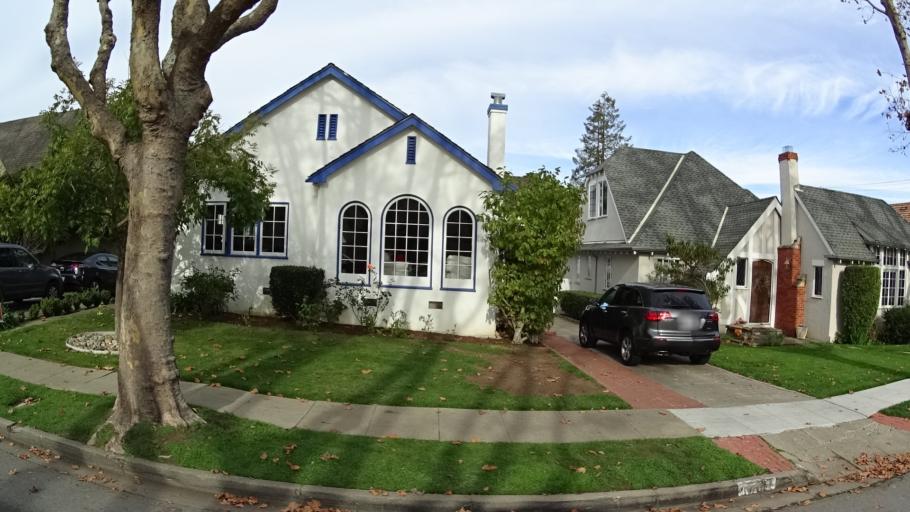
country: US
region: California
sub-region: San Mateo County
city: Burlingame
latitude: 37.5843
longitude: -122.3754
